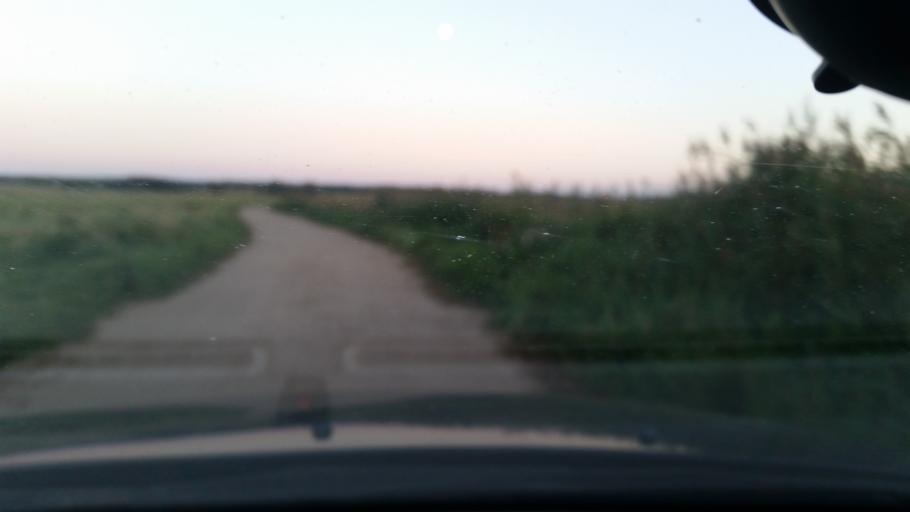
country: PL
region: Pomeranian Voivodeship
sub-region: Powiat wejherowski
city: Choczewo
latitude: 54.7883
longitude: 17.7941
